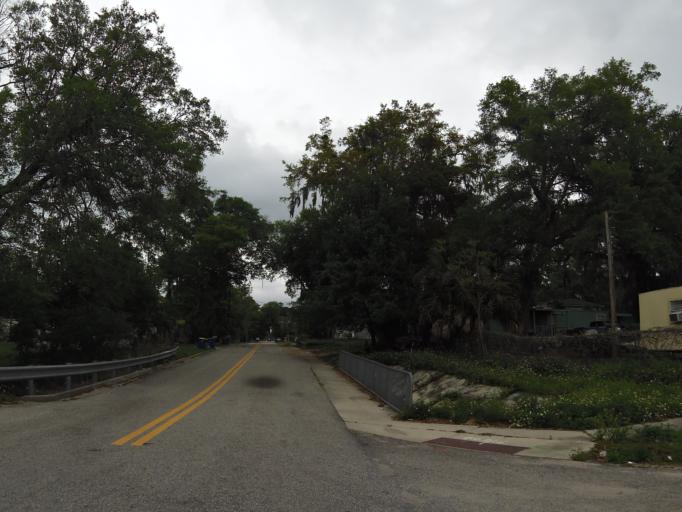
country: US
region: Florida
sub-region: Duval County
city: Jacksonville
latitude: 30.3189
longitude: -81.5660
